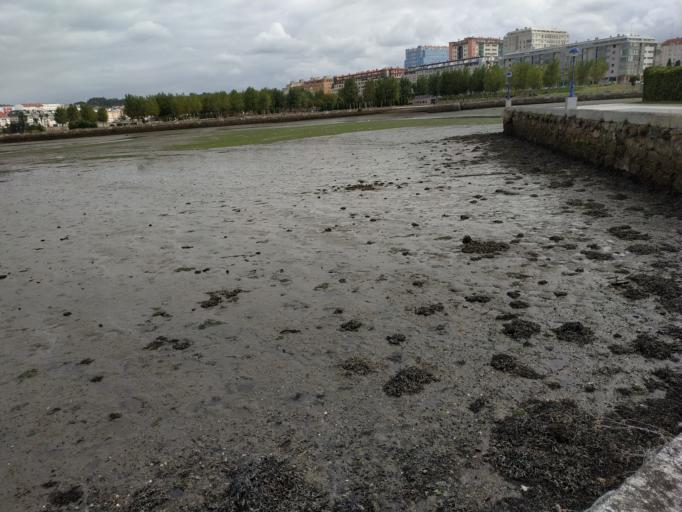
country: ES
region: Galicia
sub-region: Provincia da Coruna
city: Cambre
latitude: 43.3206
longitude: -8.3704
